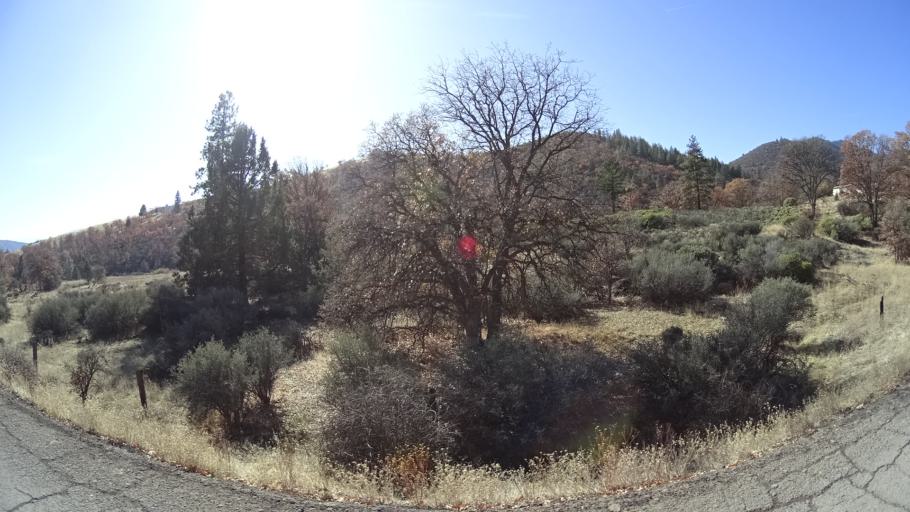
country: US
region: California
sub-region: Siskiyou County
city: Yreka
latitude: 41.7699
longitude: -122.6388
